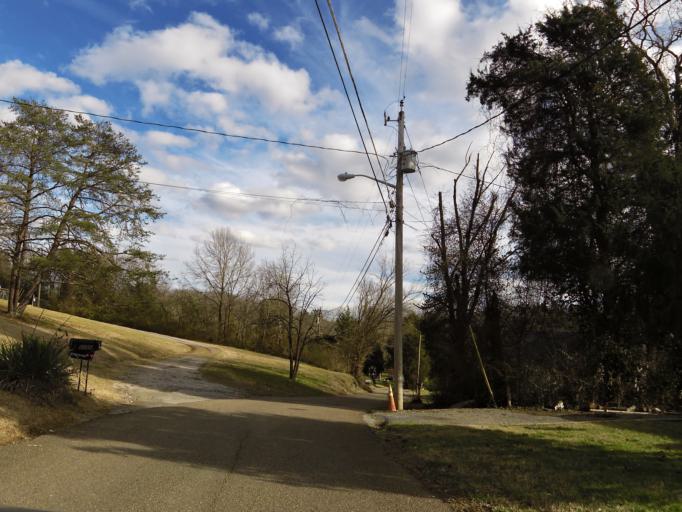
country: US
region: Tennessee
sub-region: Knox County
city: Knoxville
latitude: 35.9348
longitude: -83.8678
